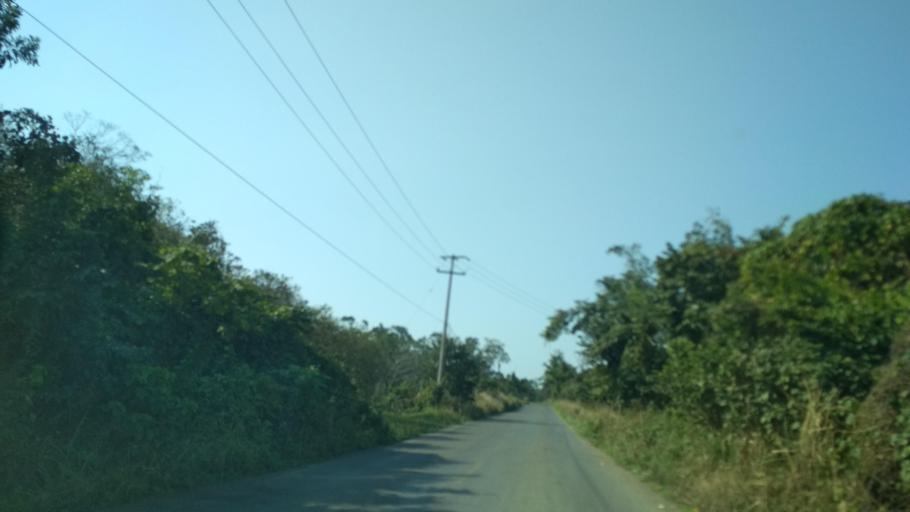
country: MX
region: Veracruz
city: Agua Dulce
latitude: 20.3968
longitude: -97.2125
